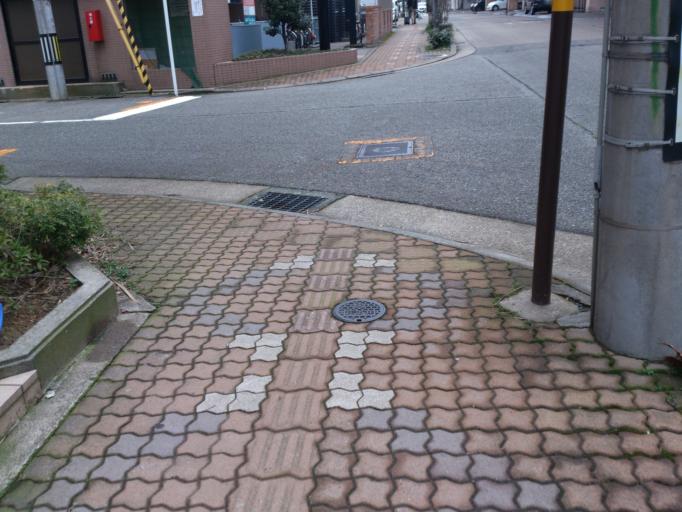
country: JP
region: Ishikawa
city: Kanazawa-shi
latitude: 36.5757
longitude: 136.6458
